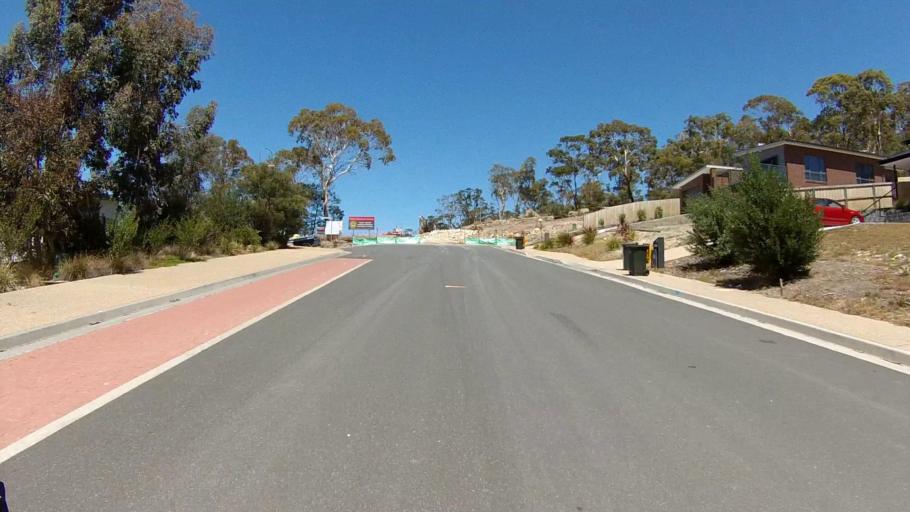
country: AU
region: Tasmania
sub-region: Clarence
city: Rokeby
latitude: -42.9078
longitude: 147.4287
